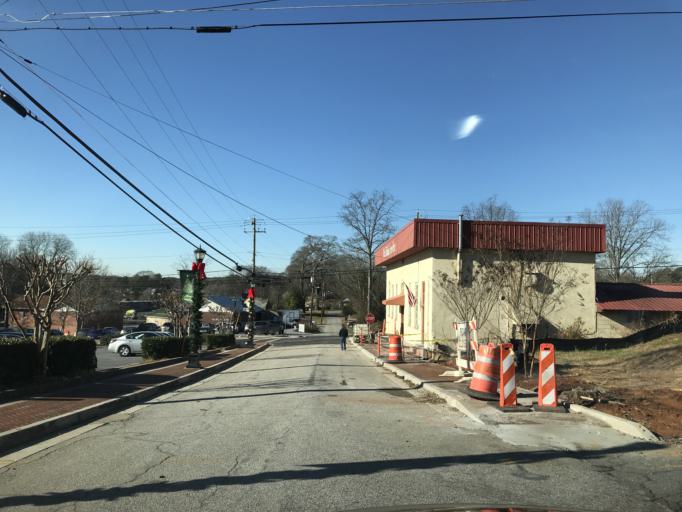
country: US
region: Georgia
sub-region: Paulding County
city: Dallas
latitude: 33.9230
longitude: -84.8409
